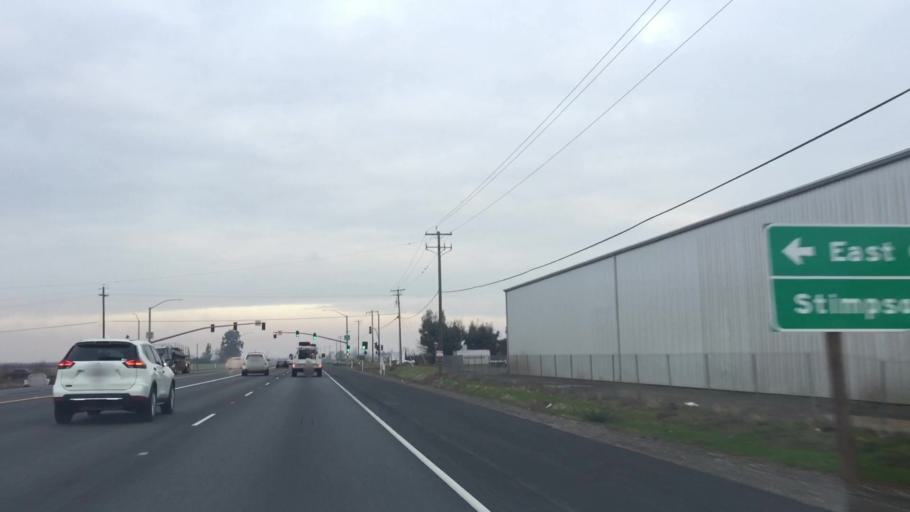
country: US
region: California
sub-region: Butte County
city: Gridley
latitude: 39.3633
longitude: -121.6074
